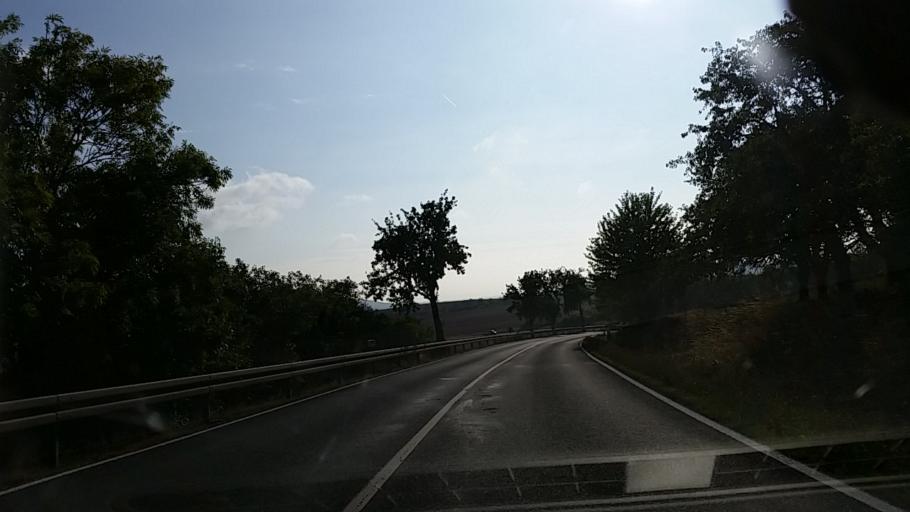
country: DE
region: Thuringia
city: Trebra
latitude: 51.3623
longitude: 10.9896
